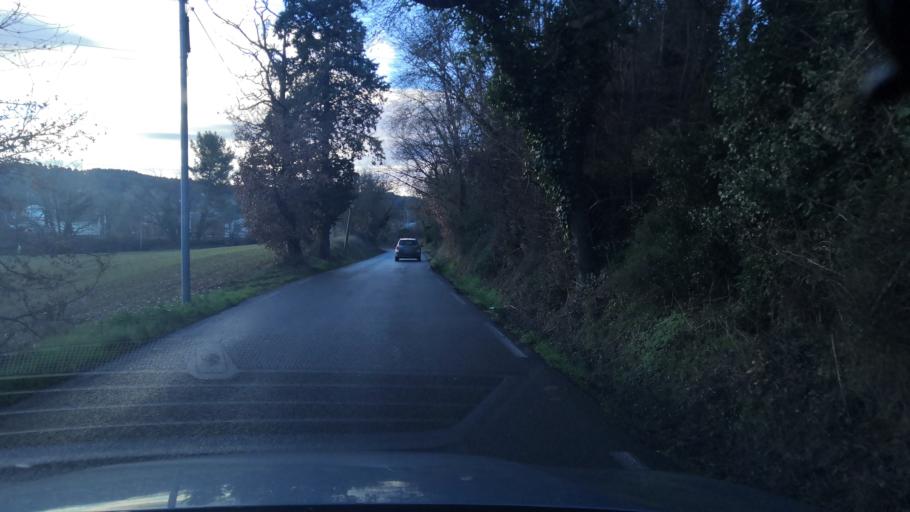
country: FR
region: Provence-Alpes-Cote d'Azur
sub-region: Departement des Bouches-du-Rhone
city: Aix-en-Provence
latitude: 43.5130
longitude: 5.4091
